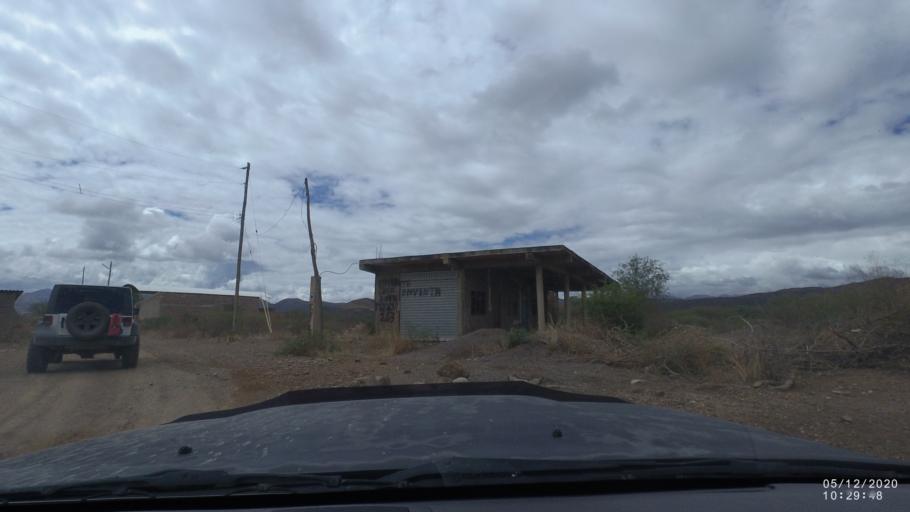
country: BO
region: Cochabamba
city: Sipe Sipe
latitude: -17.5413
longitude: -66.2698
